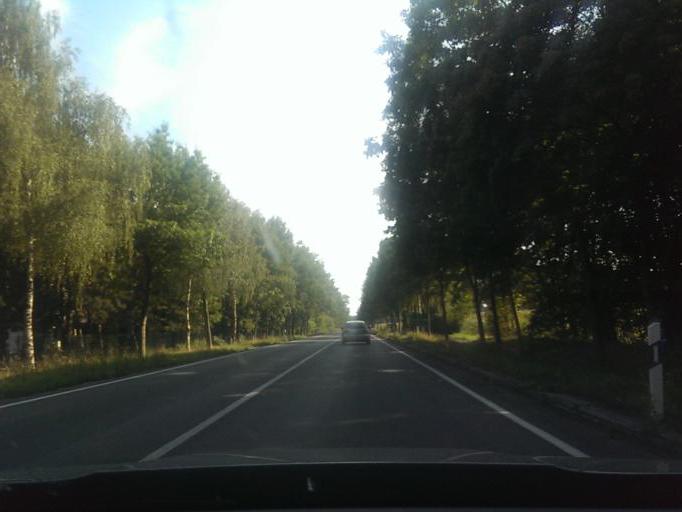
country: DE
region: North Rhine-Westphalia
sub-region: Regierungsbezirk Detmold
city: Delbruck
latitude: 51.7434
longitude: 8.5607
